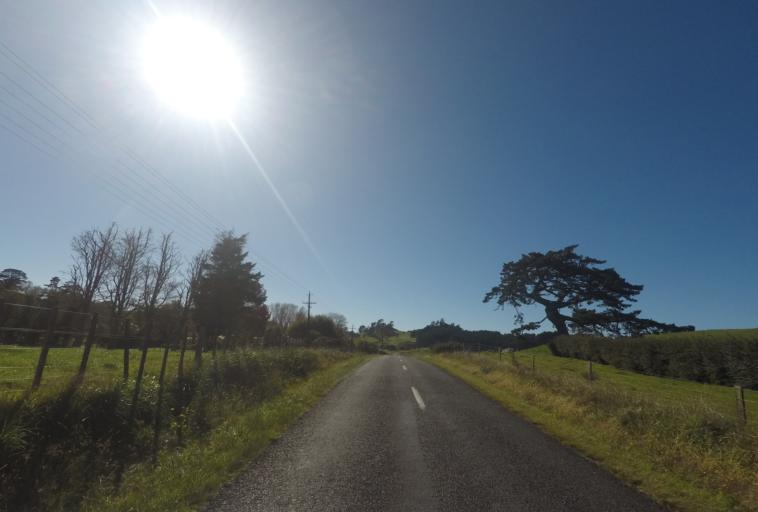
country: NZ
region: Bay of Plenty
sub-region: Western Bay of Plenty District
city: Waihi Beach
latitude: -37.4087
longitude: 175.8977
